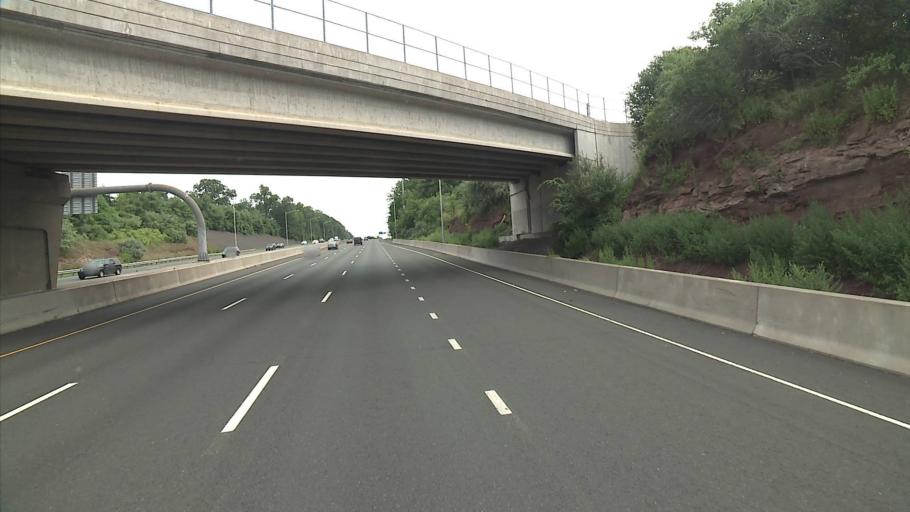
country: US
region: Connecticut
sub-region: New Haven County
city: Cheshire Village
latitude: 41.5686
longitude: -72.9097
